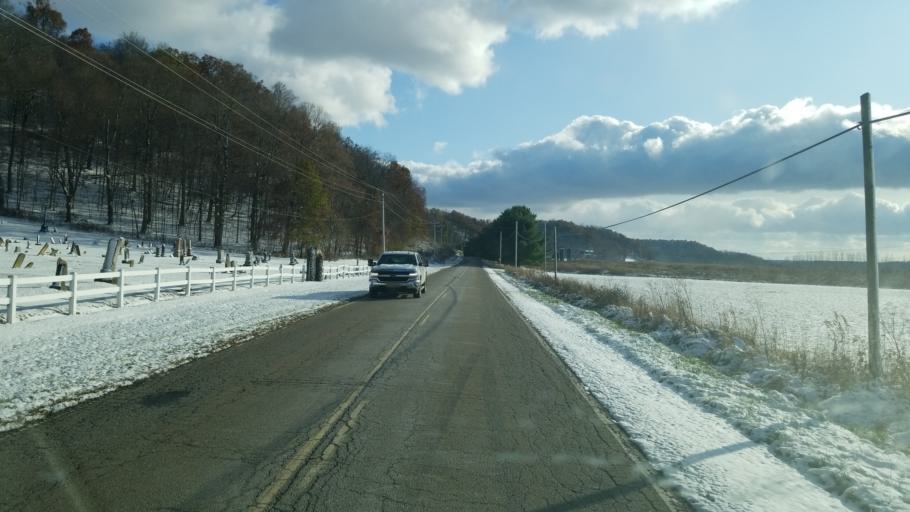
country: US
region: Ohio
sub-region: Licking County
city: Utica
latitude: 40.1633
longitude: -82.4061
